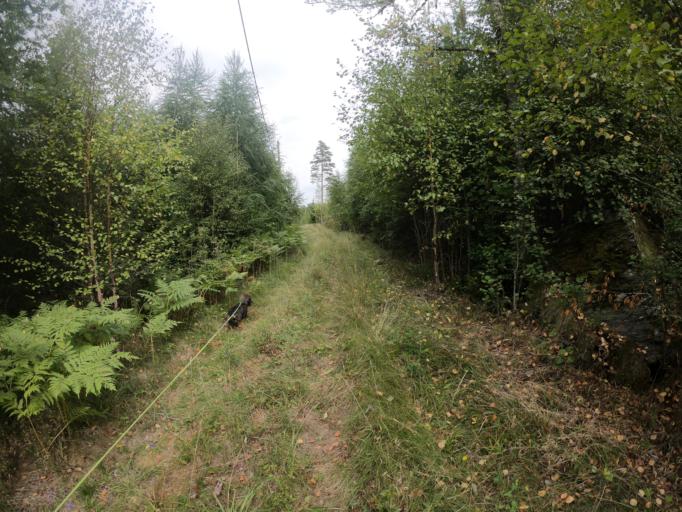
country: SE
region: Joenkoeping
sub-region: Vetlanda Kommun
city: Landsbro
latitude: 57.3158
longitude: 14.8599
